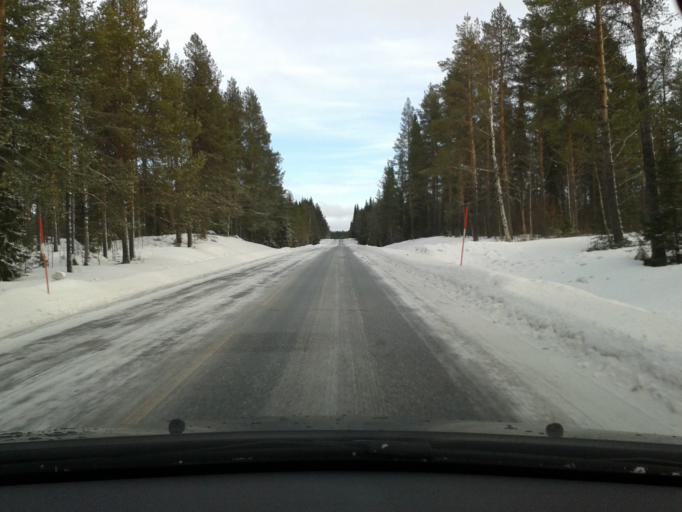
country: SE
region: Vaesterbotten
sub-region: Vilhelmina Kommun
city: Vilhelmina
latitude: 64.6426
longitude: 16.4861
